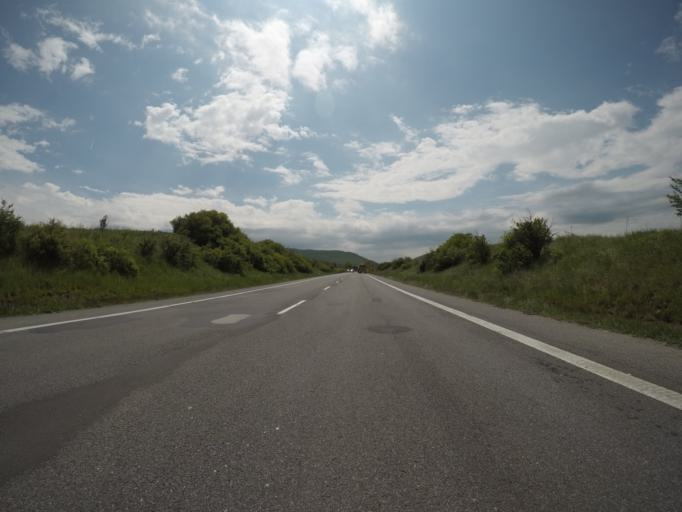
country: SK
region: Banskobystricky
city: Krupina
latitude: 48.4389
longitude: 19.0959
